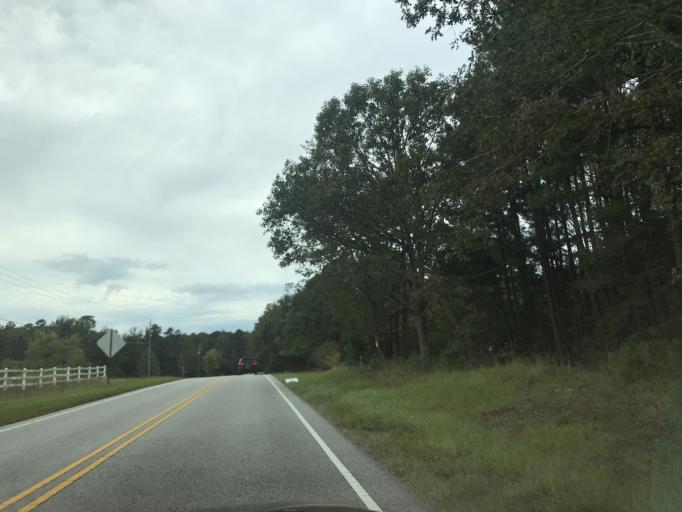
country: US
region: North Carolina
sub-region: Franklin County
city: Youngsville
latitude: 36.0029
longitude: -78.4303
